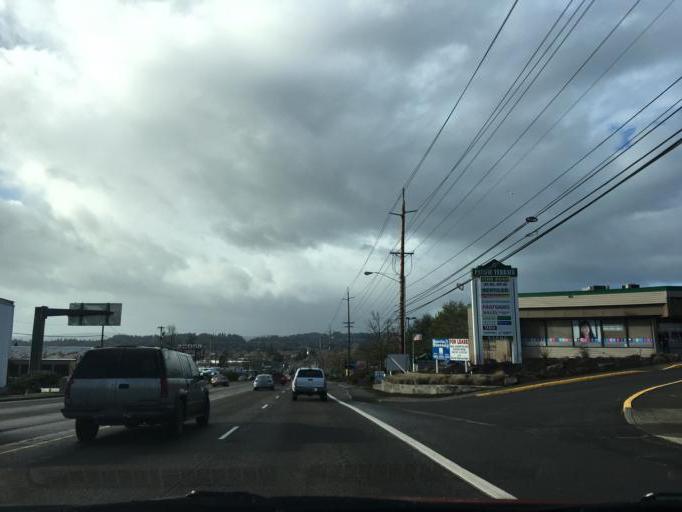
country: US
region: Oregon
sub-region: Washington County
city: Metzger
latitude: 45.4416
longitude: -122.7482
